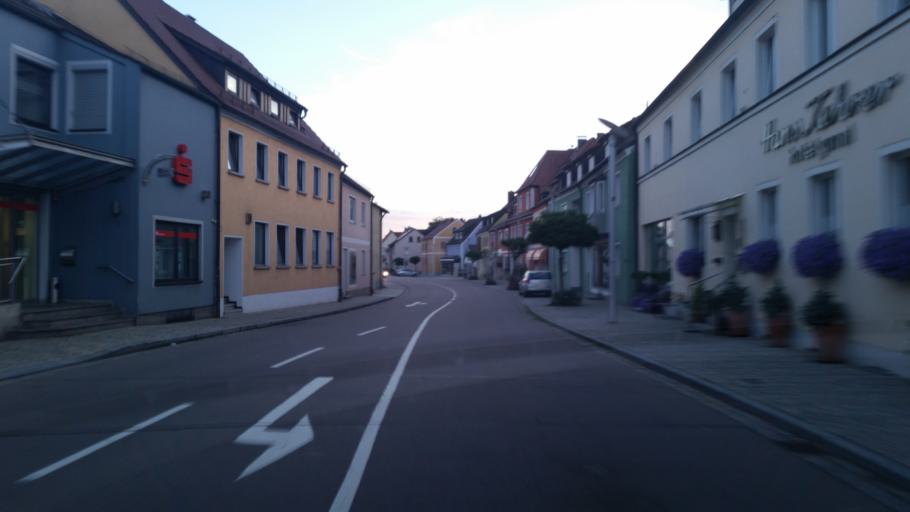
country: DE
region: Bavaria
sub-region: Upper Palatinate
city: Wernberg-Koblitz
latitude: 49.5391
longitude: 12.1599
